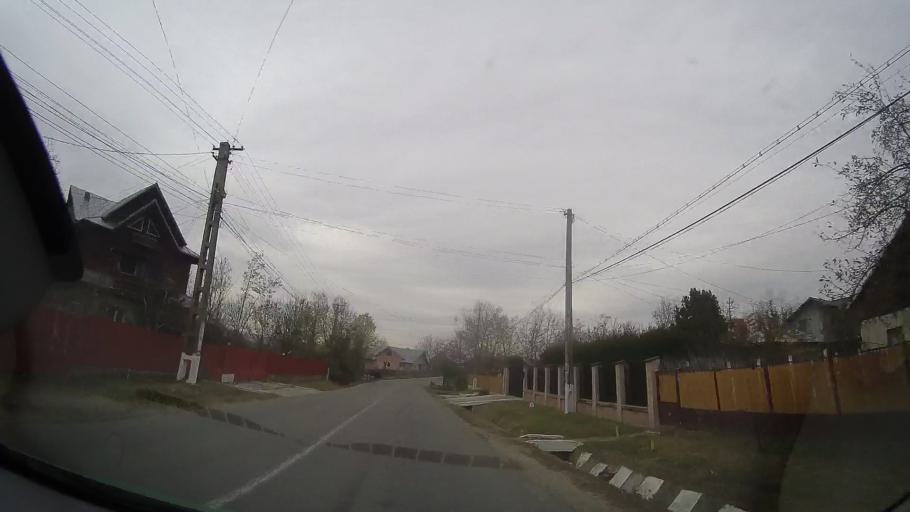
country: RO
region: Prahova
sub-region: Comuna Iordachianu
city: Iordacheanu
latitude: 45.0289
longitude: 26.2392
